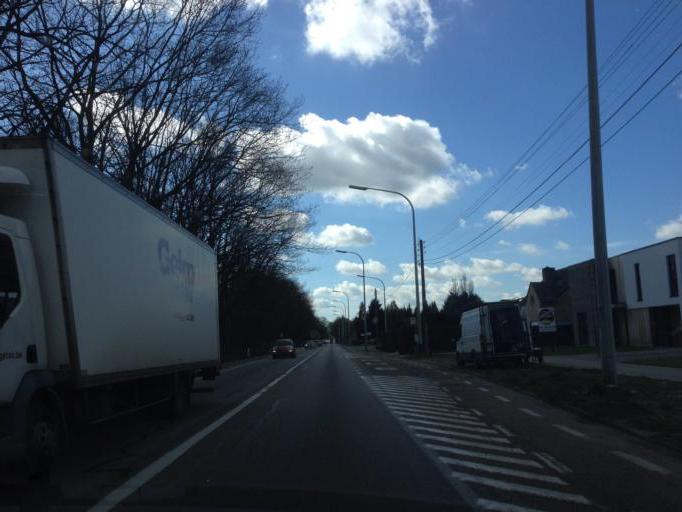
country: BE
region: Flanders
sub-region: Provincie Limburg
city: Helchteren
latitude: 51.0714
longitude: 5.3812
